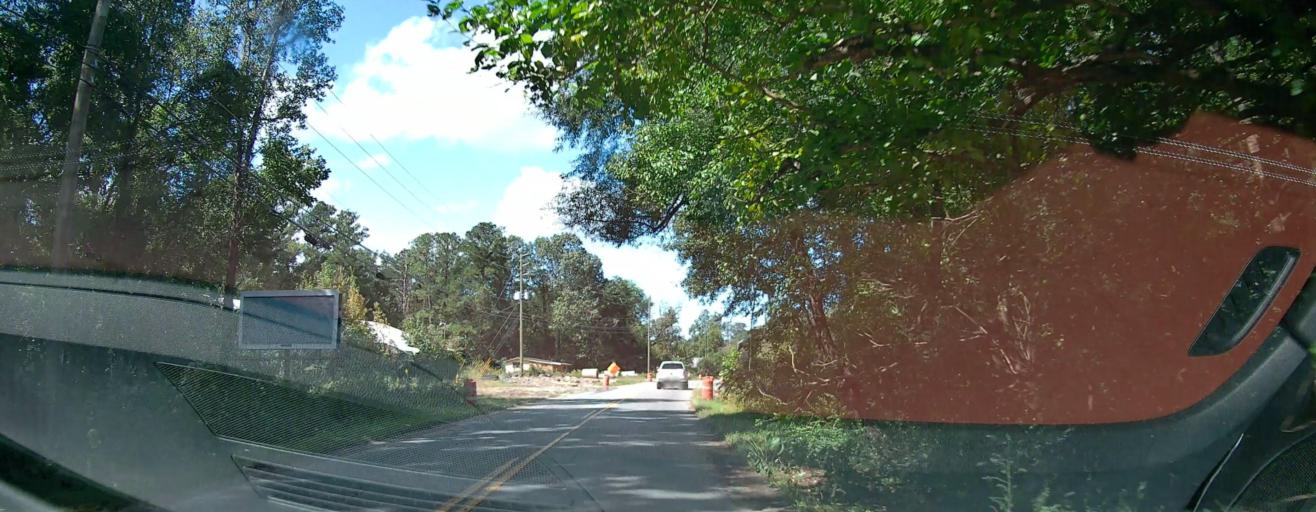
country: US
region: Georgia
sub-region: Bibb County
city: Macon
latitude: 32.8495
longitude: -83.5817
